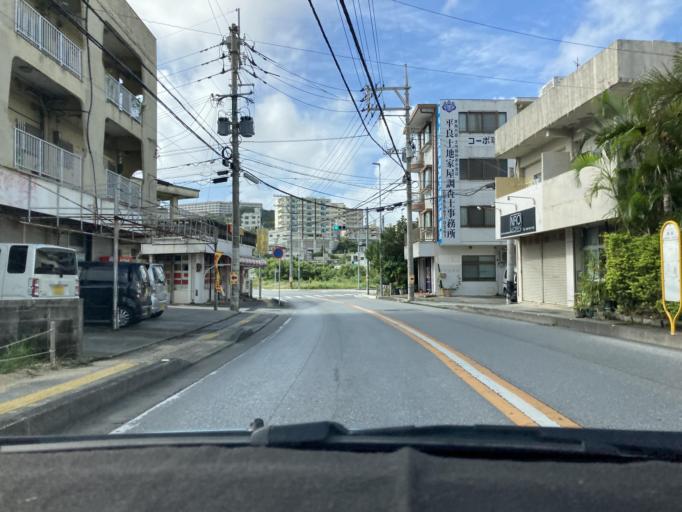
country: JP
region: Okinawa
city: Tomigusuku
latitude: 26.1796
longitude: 127.6847
